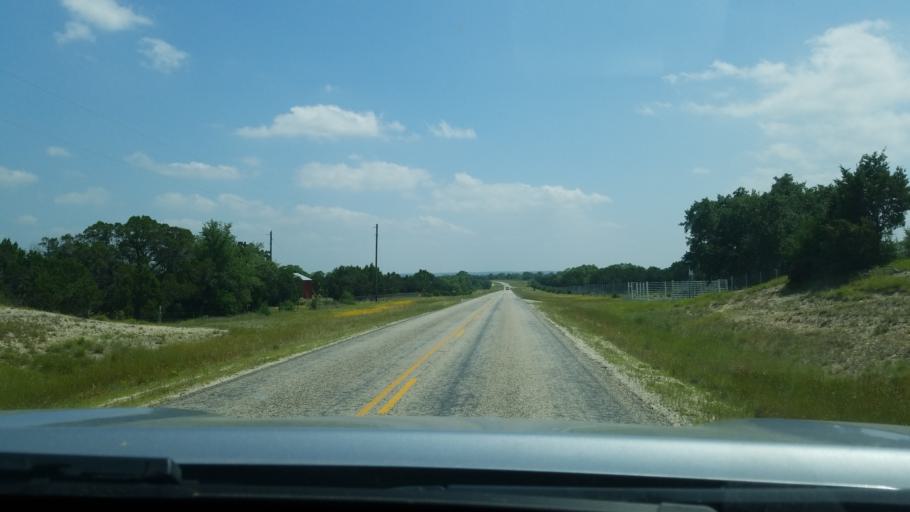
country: US
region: Texas
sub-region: Bexar County
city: Fair Oaks Ranch
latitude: 29.9149
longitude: -98.5699
